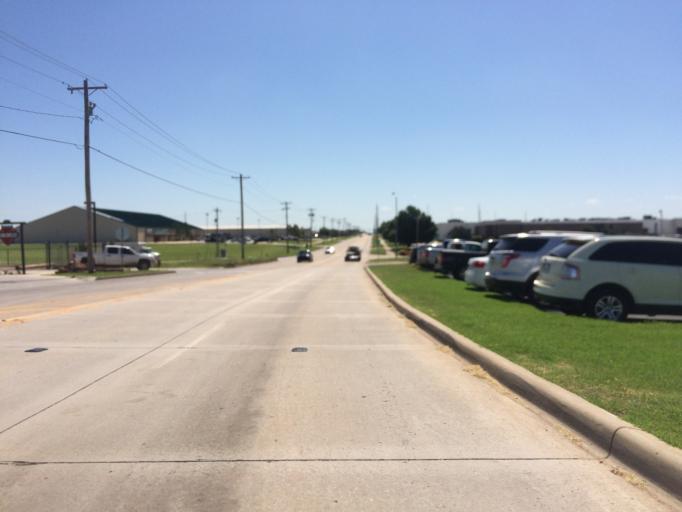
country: US
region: Oklahoma
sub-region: Cleveland County
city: Norman
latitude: 35.2474
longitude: -97.4602
